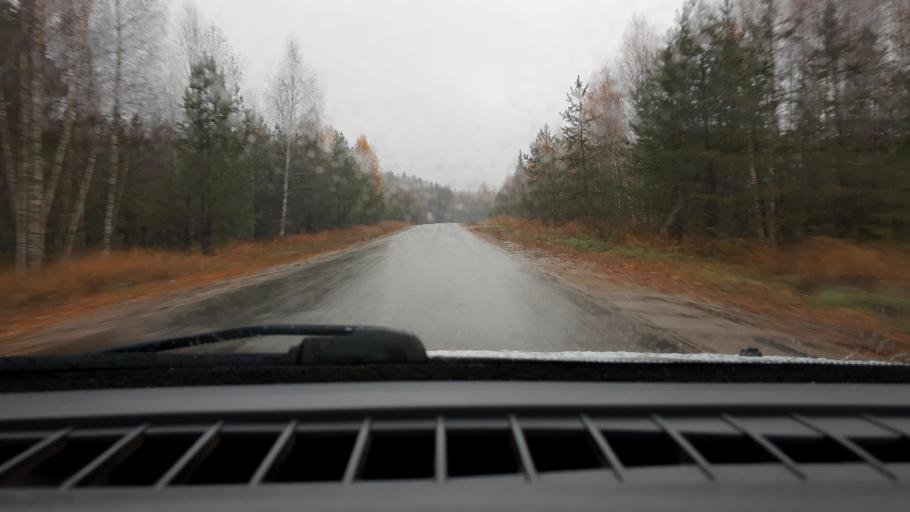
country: RU
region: Nizjnij Novgorod
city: Linda
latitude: 56.6948
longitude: 44.2057
